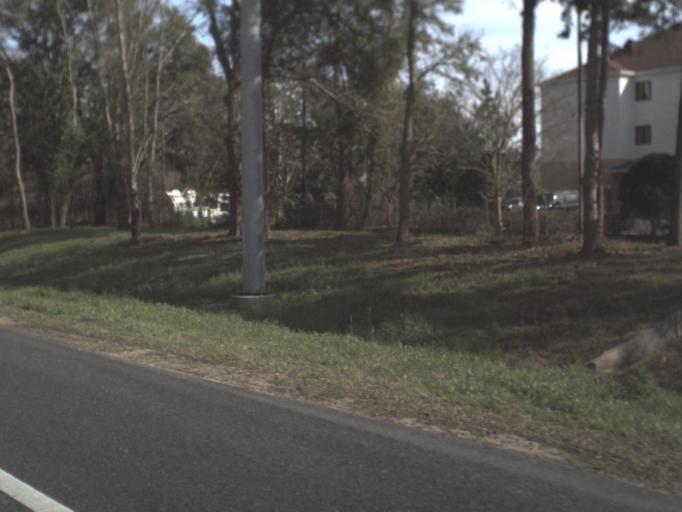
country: US
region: Florida
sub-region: Leon County
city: Tallahassee
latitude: 30.5016
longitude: -84.2448
